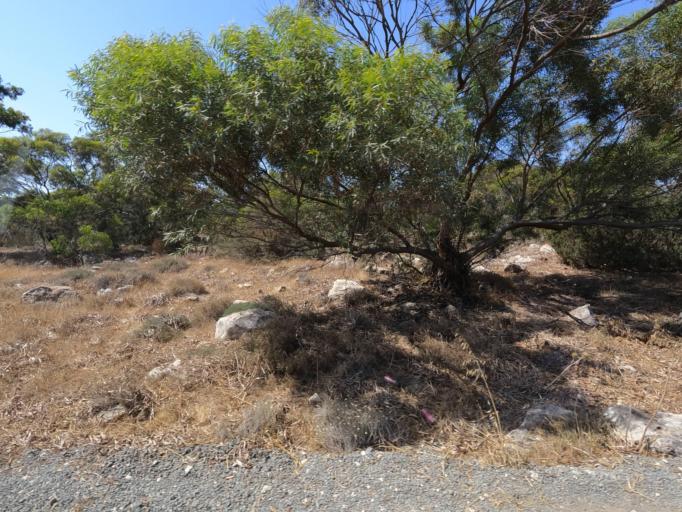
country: CY
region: Ammochostos
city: Ayia Napa
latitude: 35.0038
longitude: 33.9747
